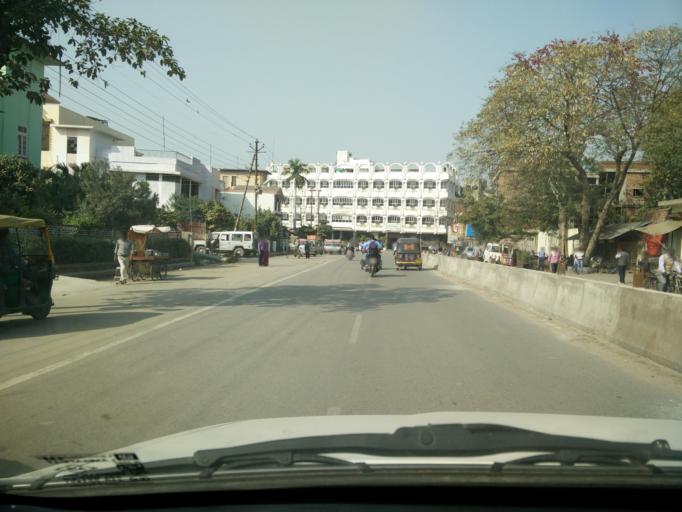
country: IN
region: Uttar Pradesh
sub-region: Varanasi
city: Varanasi
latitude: 25.2959
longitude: 83.0025
